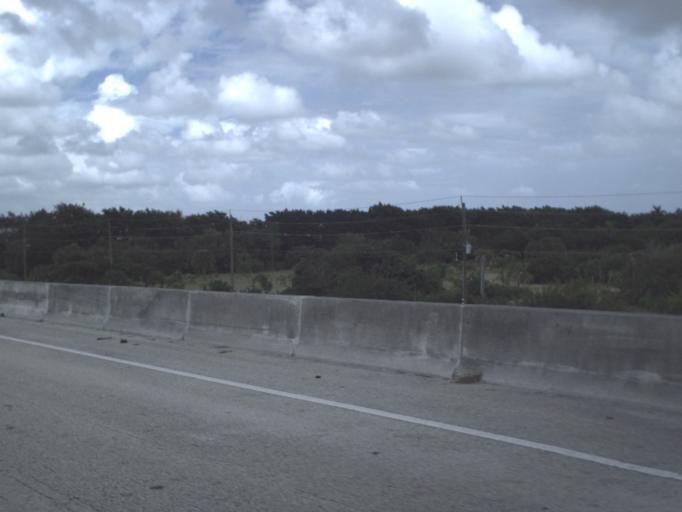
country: US
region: Florida
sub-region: Palm Beach County
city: Villages of Oriole
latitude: 26.5285
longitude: -80.1725
